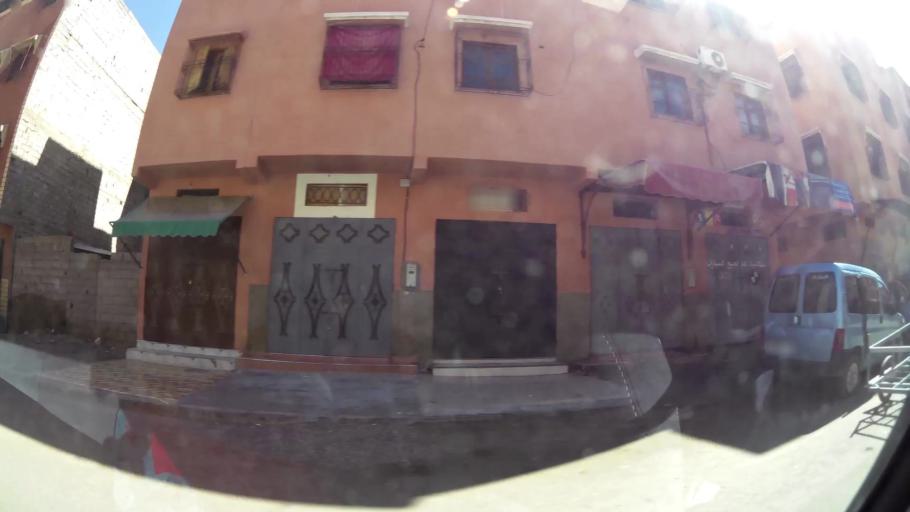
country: MA
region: Marrakech-Tensift-Al Haouz
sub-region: Marrakech
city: Marrakesh
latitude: 31.6473
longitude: -7.9800
